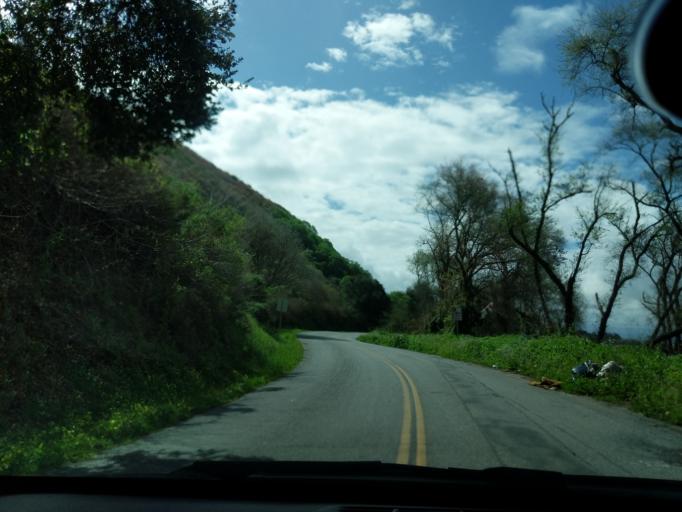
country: US
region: California
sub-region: Monterey County
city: Prunedale
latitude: 36.7681
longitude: -121.6017
